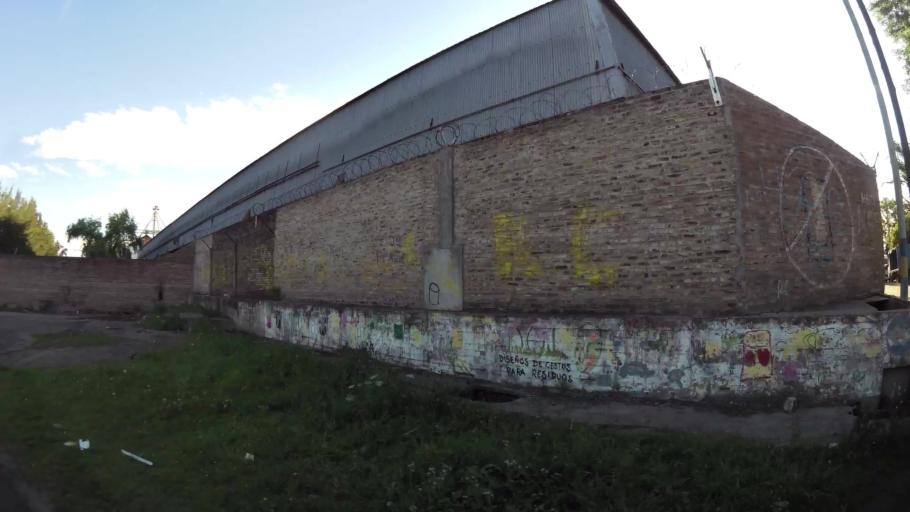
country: AR
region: Santa Fe
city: Gobernador Galvez
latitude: -32.9884
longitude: -60.6805
